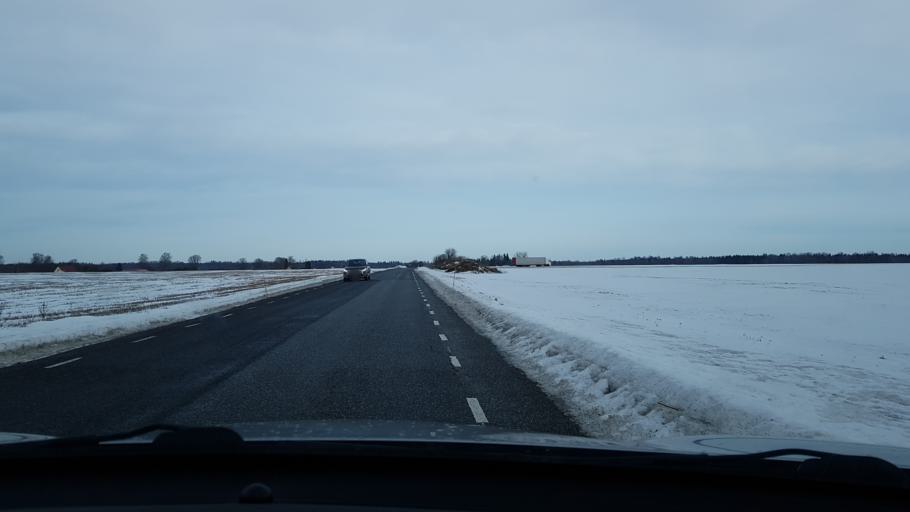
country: EE
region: Jaervamaa
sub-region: Paide linn
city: Paide
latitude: 58.8757
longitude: 25.6720
